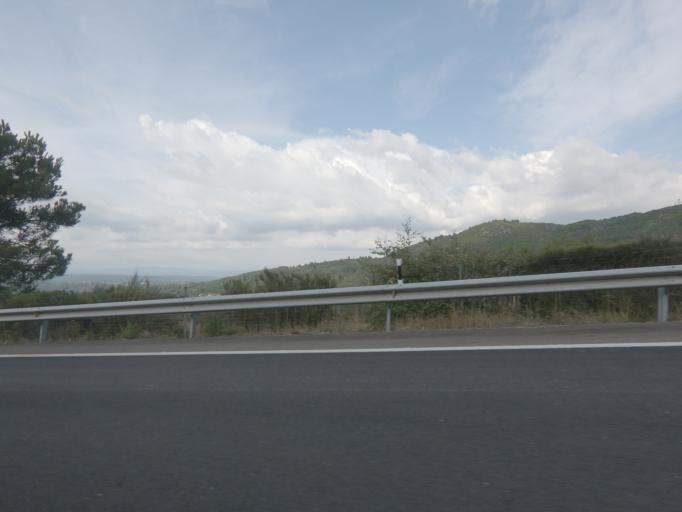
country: ES
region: Galicia
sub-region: Provincia de Ourense
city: Ambia
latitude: 42.1837
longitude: -7.7651
